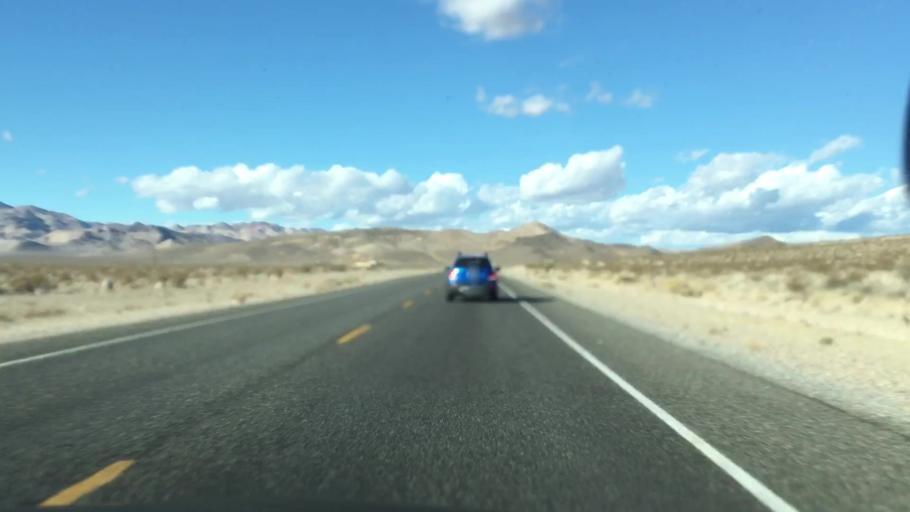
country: US
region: Nevada
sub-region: Nye County
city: Beatty
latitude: 36.8530
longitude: -116.7563
